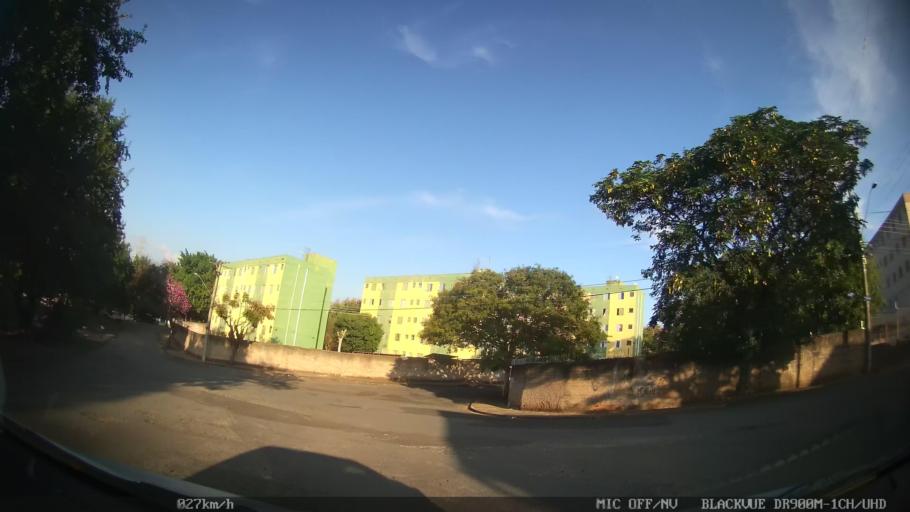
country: BR
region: Sao Paulo
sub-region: Campinas
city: Campinas
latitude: -22.9749
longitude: -47.1175
